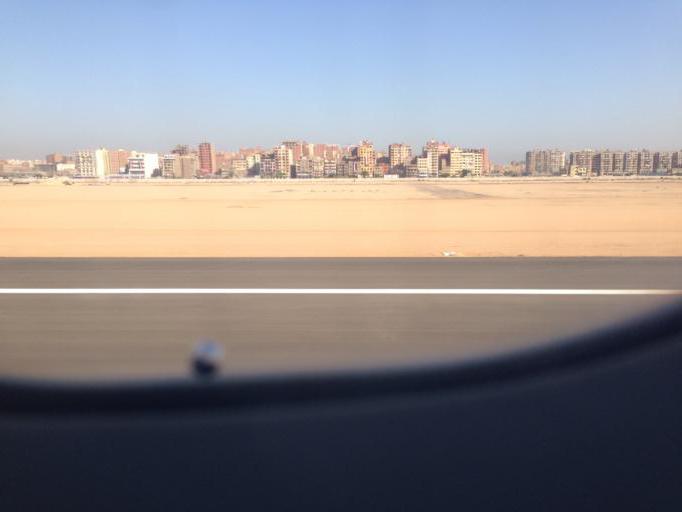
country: EG
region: Muhafazat al Qalyubiyah
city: Al Khankah
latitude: 30.1306
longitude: 31.3949
